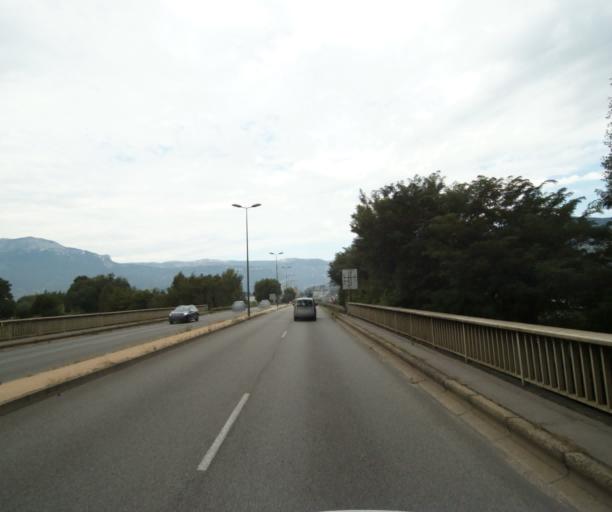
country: FR
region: Rhone-Alpes
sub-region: Departement de l'Isere
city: Gieres
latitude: 45.1827
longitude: 5.7757
